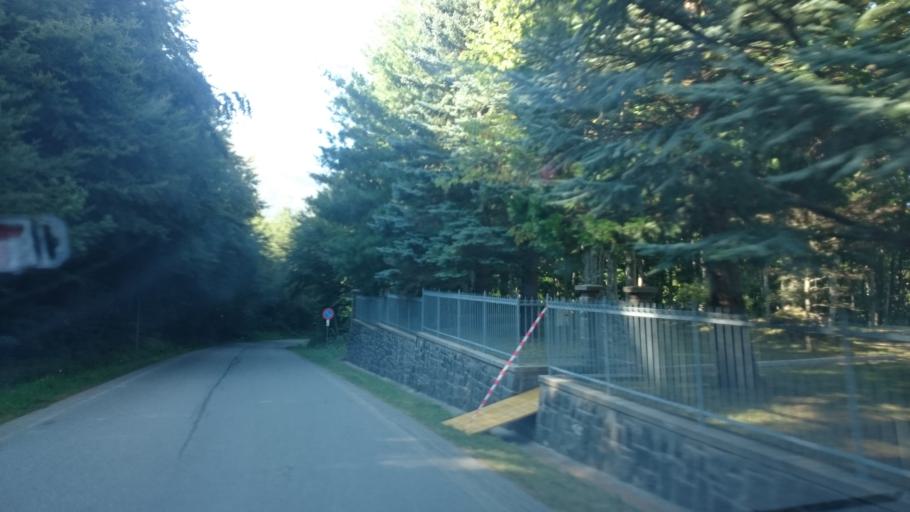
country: IT
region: Emilia-Romagna
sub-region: Provincia di Reggio Emilia
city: Villa Minozzo
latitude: 44.3002
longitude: 10.4297
